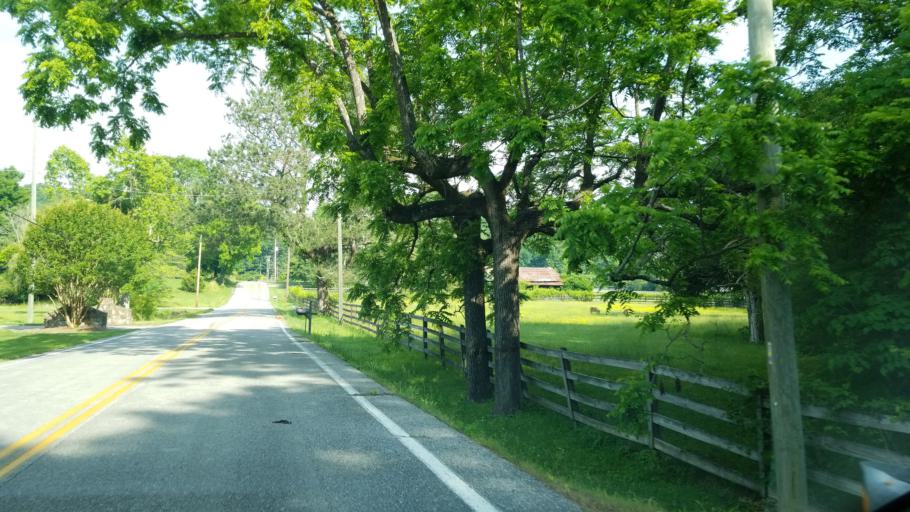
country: US
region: Tennessee
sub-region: Hamilton County
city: Collegedale
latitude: 35.0992
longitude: -85.0166
